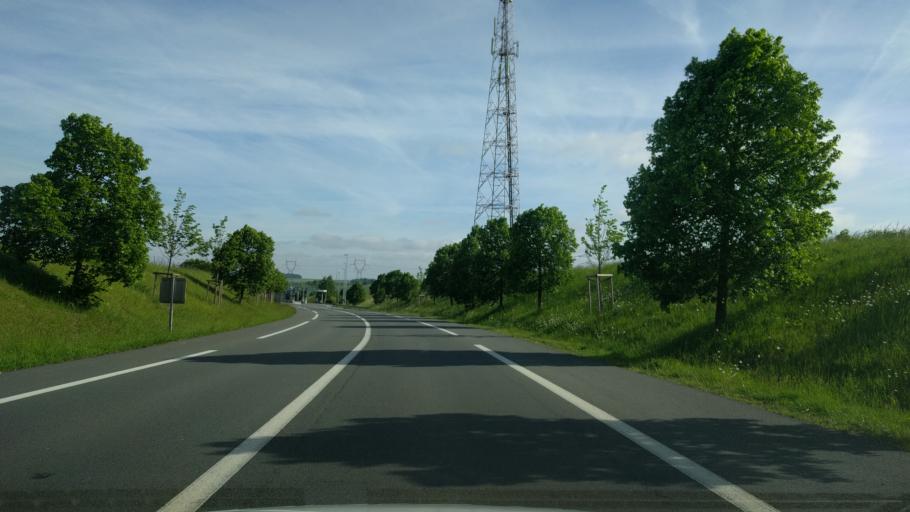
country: FR
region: Picardie
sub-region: Departement de la Somme
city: Peronne
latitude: 49.9630
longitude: 2.8632
